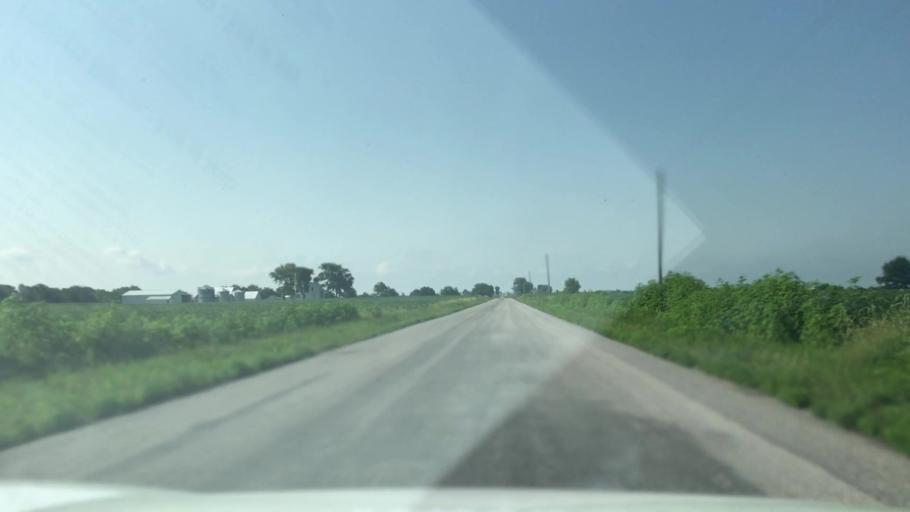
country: US
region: Illinois
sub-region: Washington County
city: Okawville
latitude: 38.4415
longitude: -89.4779
